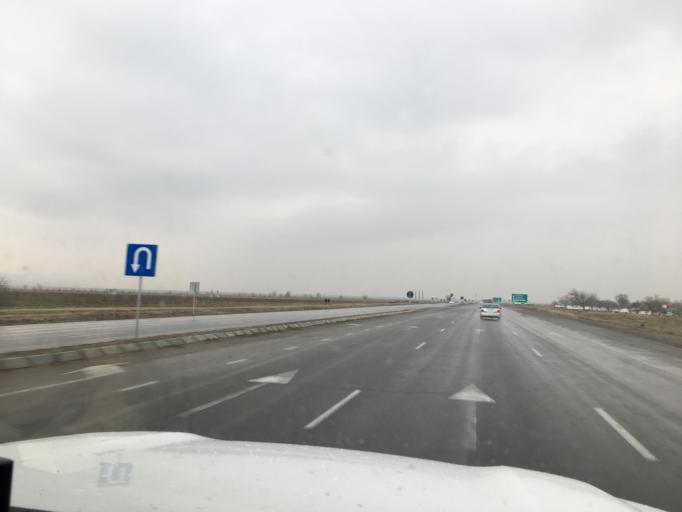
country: TM
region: Ahal
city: Annau
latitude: 37.8264
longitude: 58.7530
